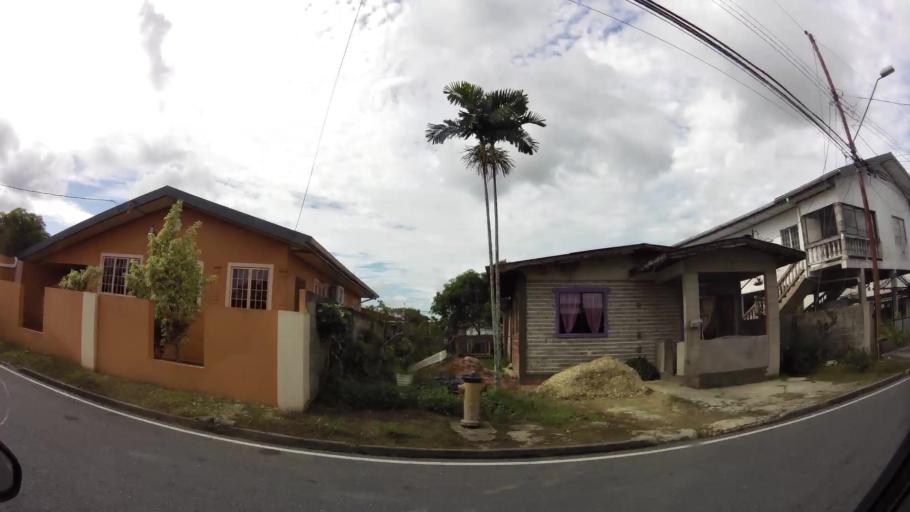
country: TT
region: Chaguanas
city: Chaguanas
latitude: 10.5120
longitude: -61.3949
